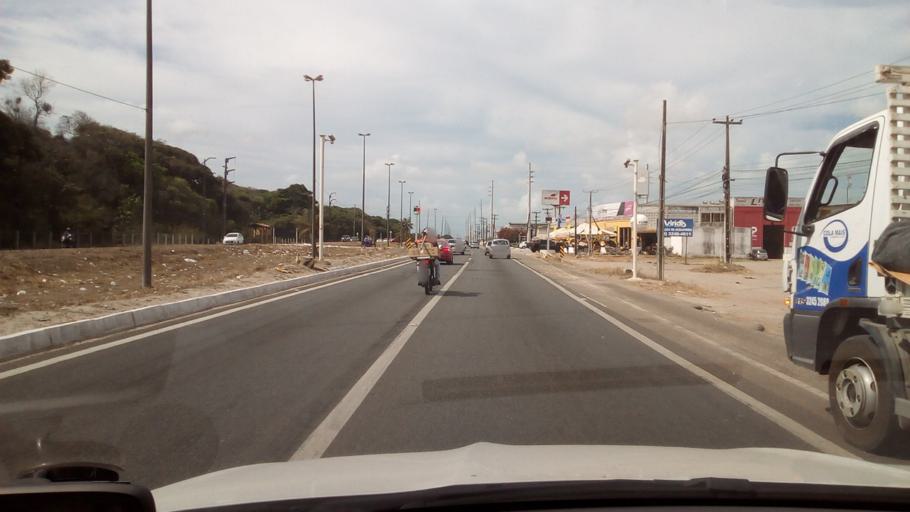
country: BR
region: Paraiba
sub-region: Joao Pessoa
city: Joao Pessoa
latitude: -7.0662
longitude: -34.8500
